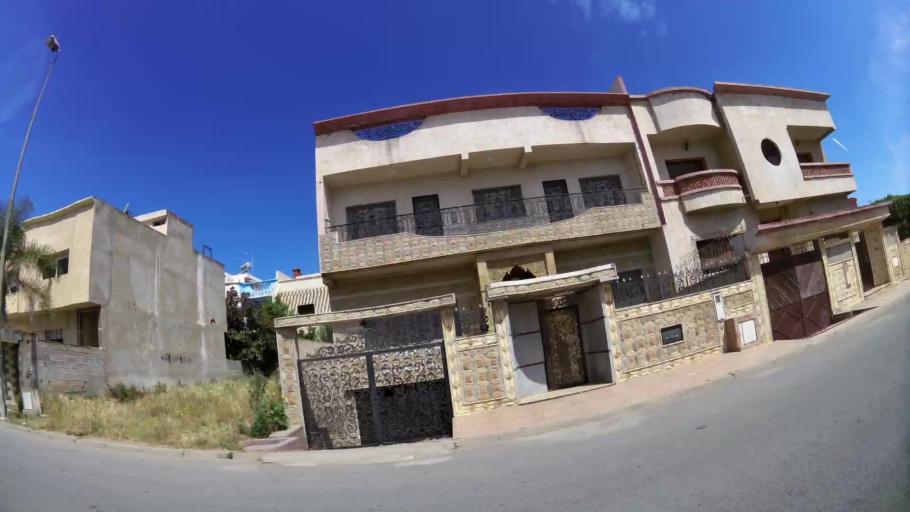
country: MA
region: Rabat-Sale-Zemmour-Zaer
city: Sale
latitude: 34.0706
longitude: -6.7898
